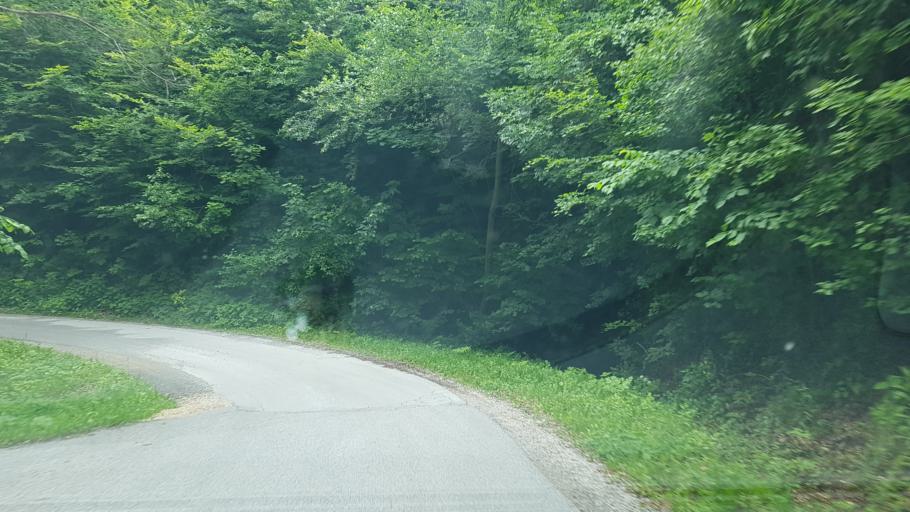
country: SI
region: Dobrna
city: Dobrna
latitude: 46.3559
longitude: 15.2439
